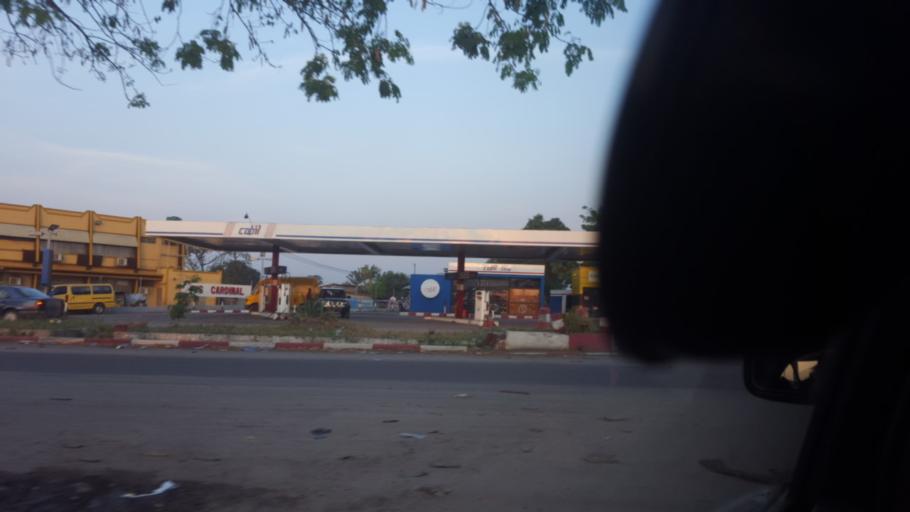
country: CD
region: Kinshasa
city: Kinshasa
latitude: -4.3445
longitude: 15.3248
